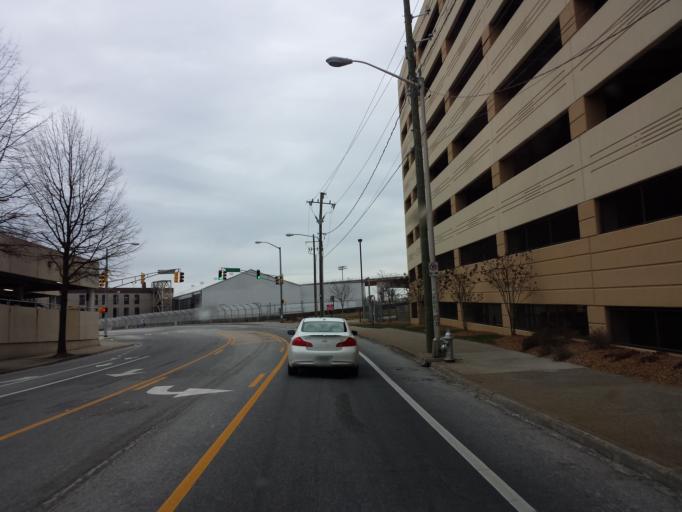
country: US
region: Georgia
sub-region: Fulton County
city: Atlanta
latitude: 33.7503
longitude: -84.3838
